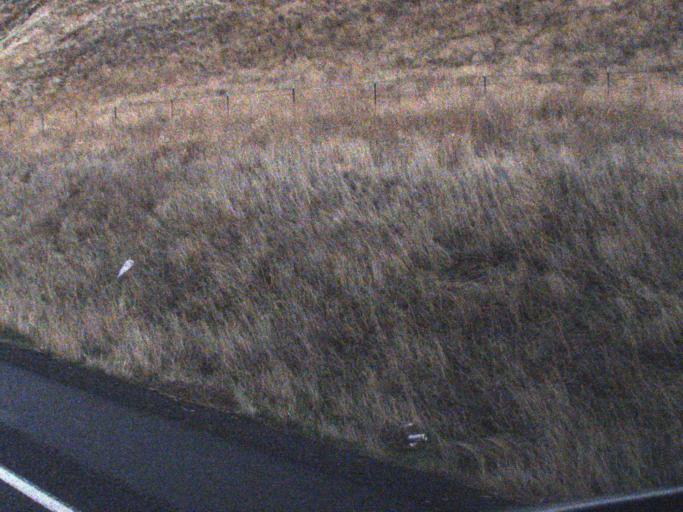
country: US
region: Washington
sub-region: Columbia County
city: Dayton
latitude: 46.5457
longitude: -117.8885
